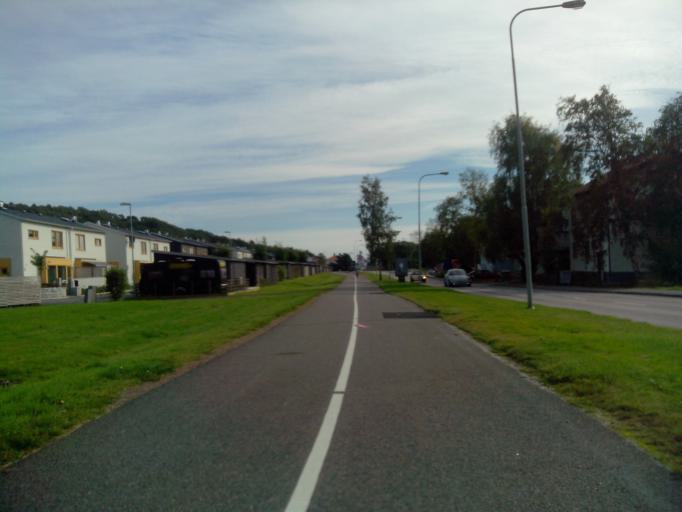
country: SE
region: Vaestra Goetaland
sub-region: Goteborg
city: Goeteborg
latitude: 57.7364
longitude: 11.9569
